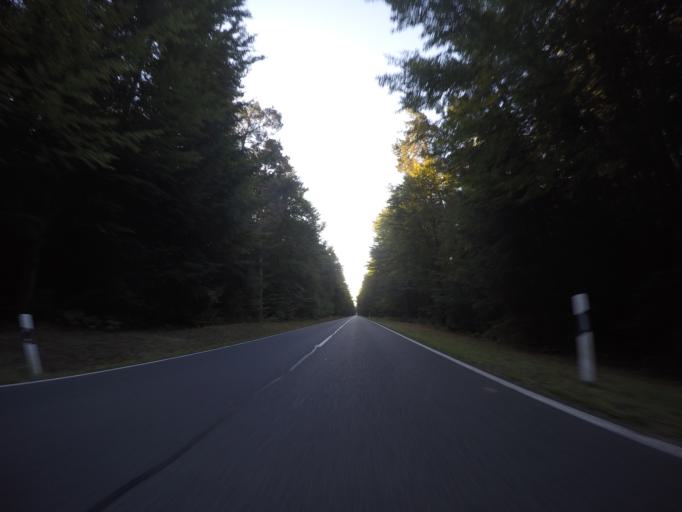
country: DE
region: Bavaria
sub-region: Regierungsbezirk Unterfranken
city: Schollbrunn
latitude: 49.8518
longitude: 9.4382
